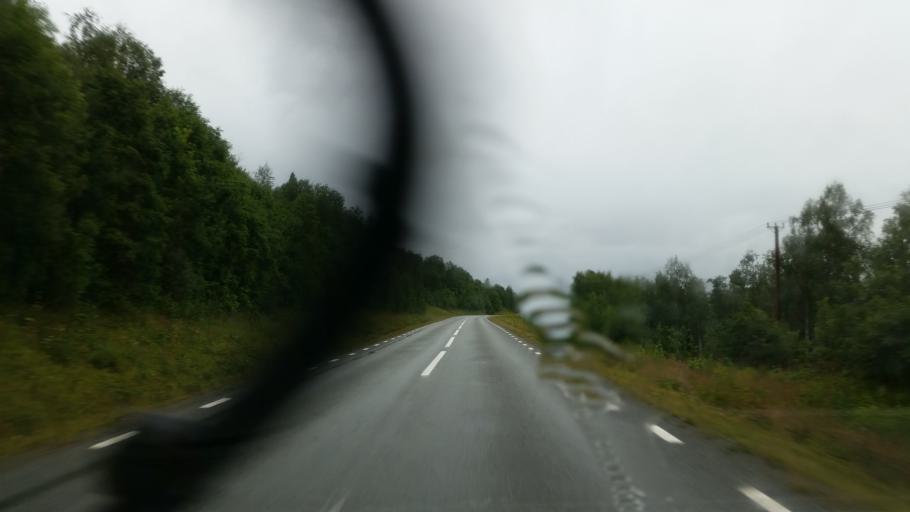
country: NO
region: Nordland
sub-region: Rana
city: Mo i Rana
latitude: 65.8559
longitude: 15.0305
